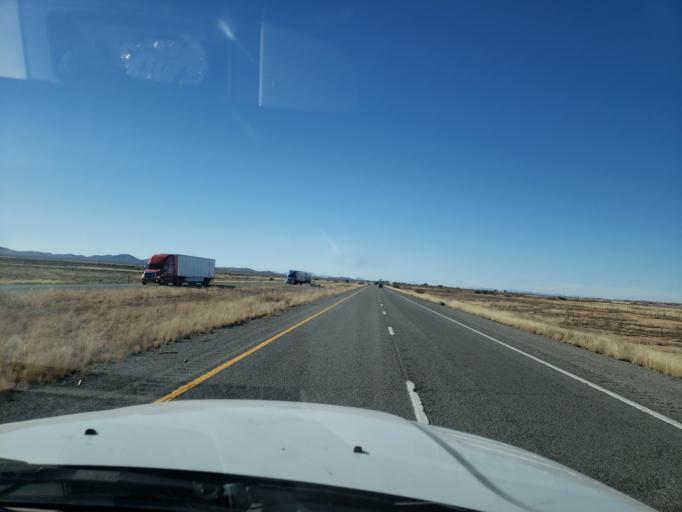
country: US
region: New Mexico
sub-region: Hidalgo County
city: Lordsburg
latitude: 32.3298
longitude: -108.6386
